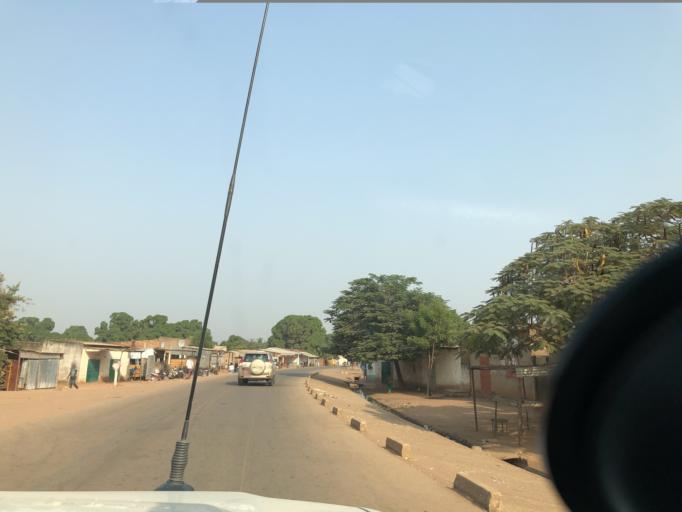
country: TD
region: Logone Occidental
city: Moundou
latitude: 8.5605
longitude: 16.0546
